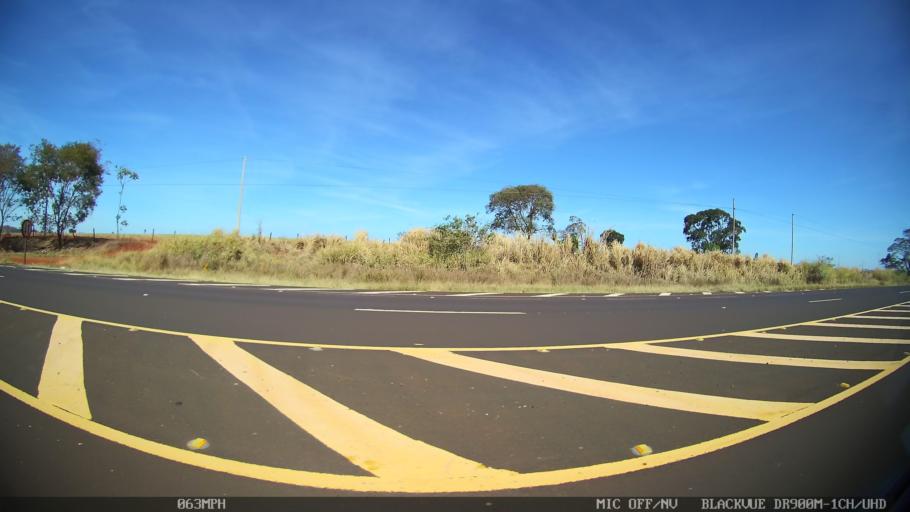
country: BR
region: Sao Paulo
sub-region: Nuporanga
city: Nuporanga
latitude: -20.5612
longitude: -47.6236
